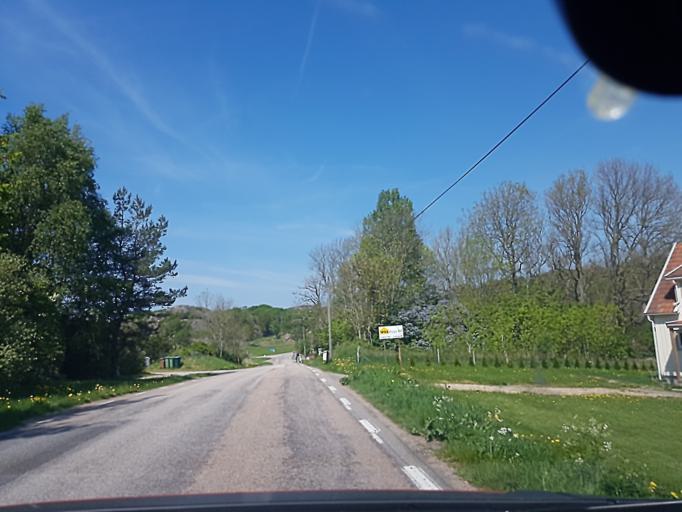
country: SE
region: Vaestra Goetaland
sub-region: Lysekils Kommun
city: Lysekil
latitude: 58.1566
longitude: 11.4612
